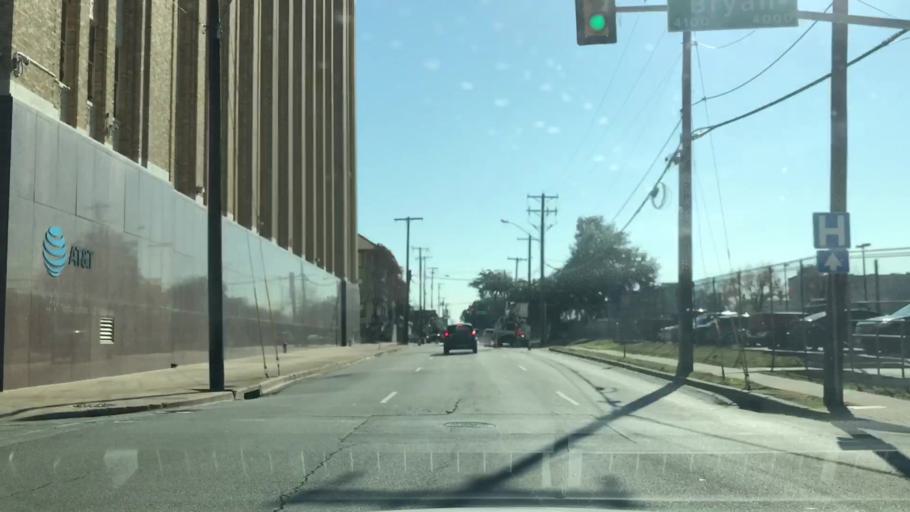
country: US
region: Texas
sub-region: Dallas County
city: Dallas
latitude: 32.7976
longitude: -96.7811
